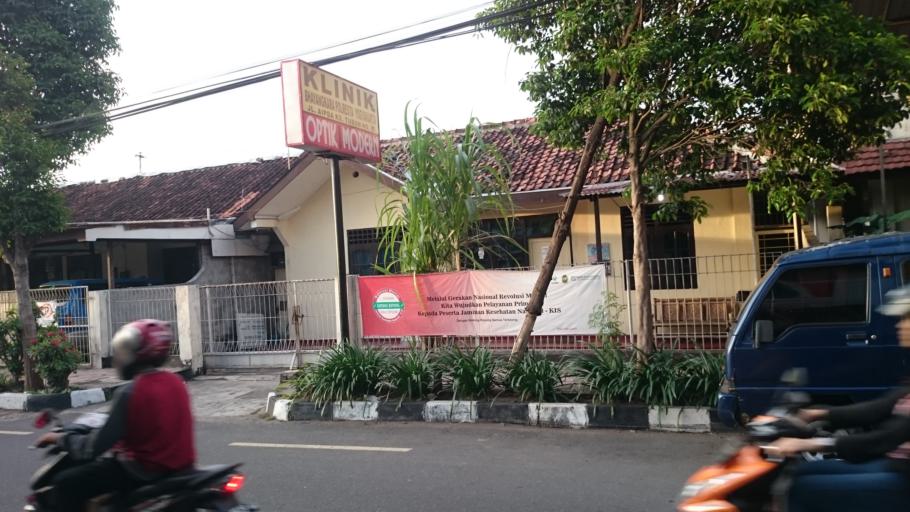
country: ID
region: Daerah Istimewa Yogyakarta
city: Yogyakarta
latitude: -7.7975
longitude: 110.3608
